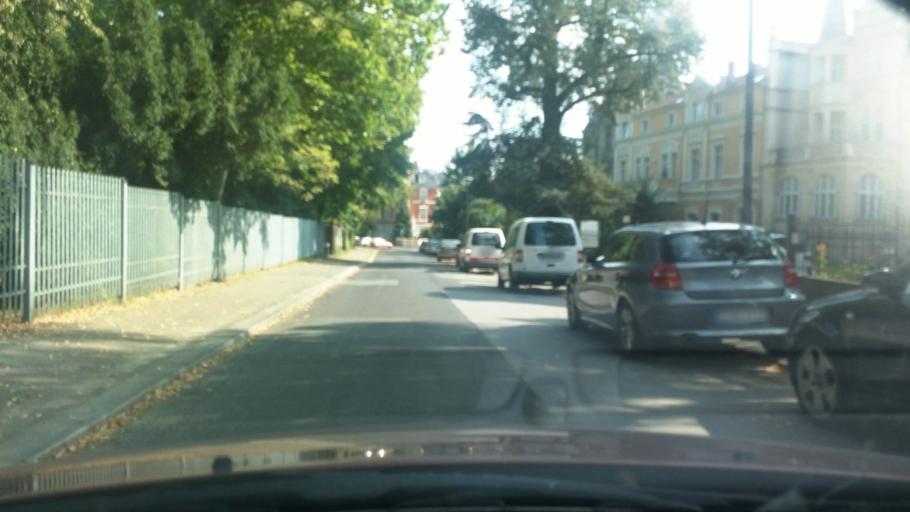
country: DE
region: Saxony
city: Goerlitz
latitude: 51.1495
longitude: 14.9924
